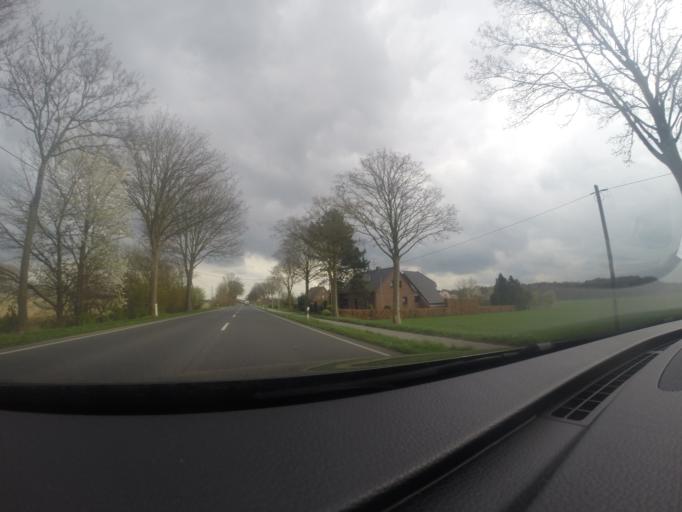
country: DE
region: North Rhine-Westphalia
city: Rees
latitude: 51.7070
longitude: 6.3565
